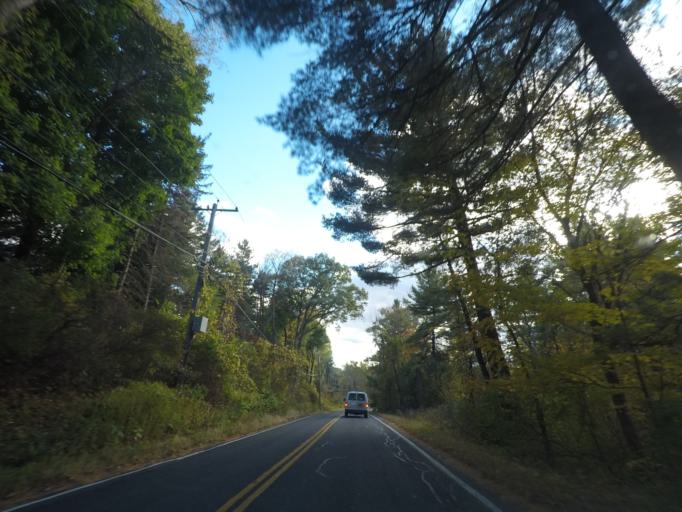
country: US
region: New York
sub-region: Schenectady County
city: Niskayuna
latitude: 42.7606
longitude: -73.8314
